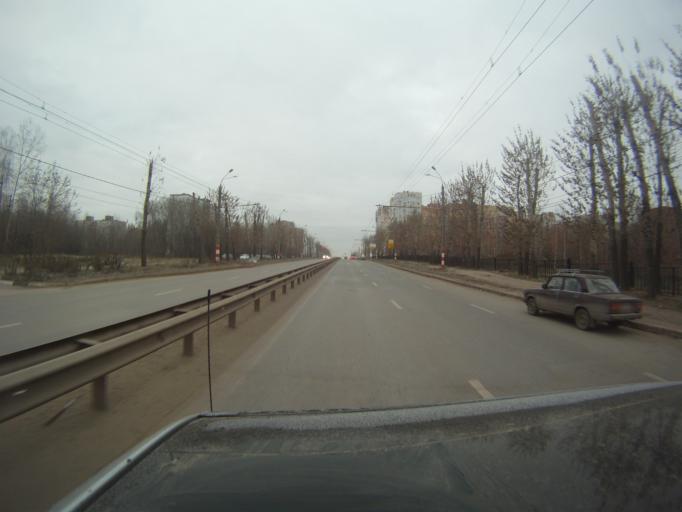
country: RU
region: Nizjnij Novgorod
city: Nizhniy Novgorod
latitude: 56.2862
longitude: 44.0361
